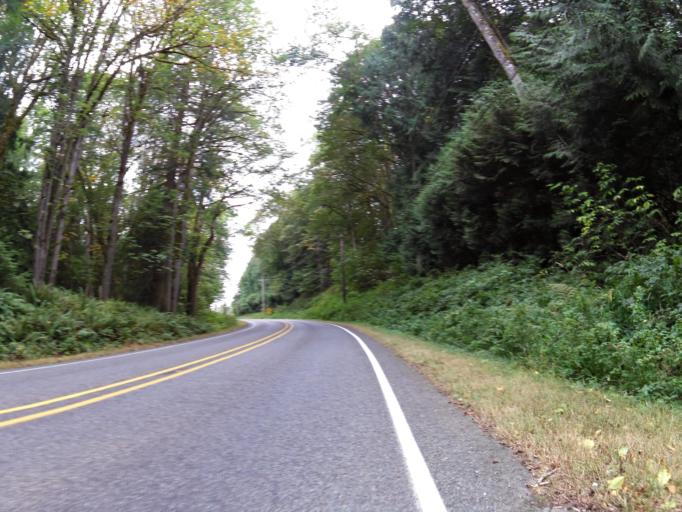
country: US
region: Washington
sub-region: Jefferson County
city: Port Ludlow
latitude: 47.9558
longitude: -122.6981
